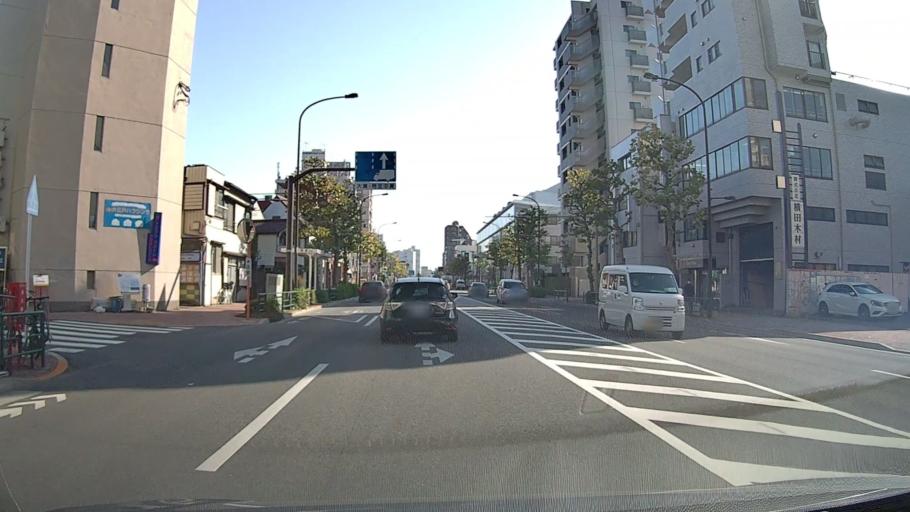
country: JP
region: Tokyo
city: Tokyo
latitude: 35.7315
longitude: 139.6733
